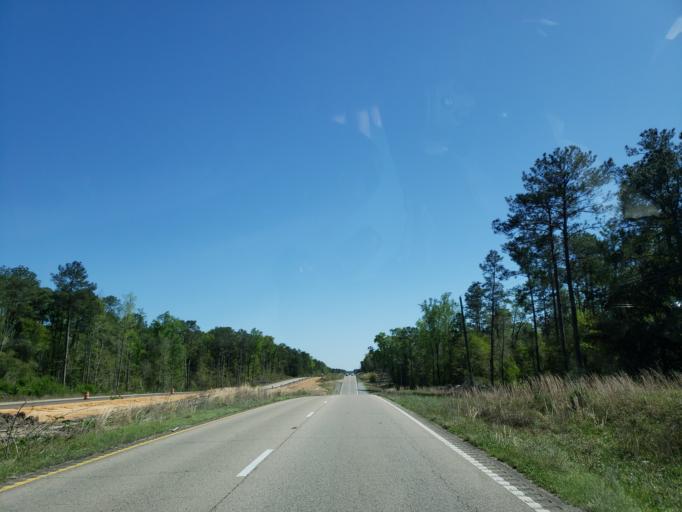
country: US
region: Mississippi
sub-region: Lamar County
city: Purvis
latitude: 31.1499
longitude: -89.2362
